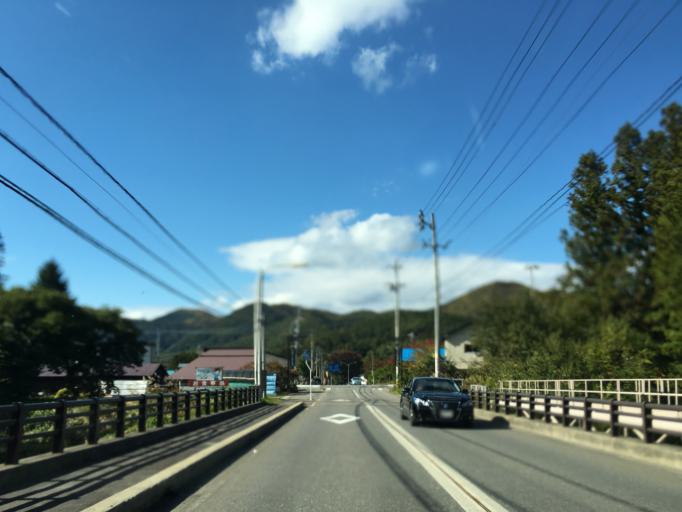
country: JP
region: Fukushima
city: Inawashiro
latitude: 37.6186
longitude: 140.2030
